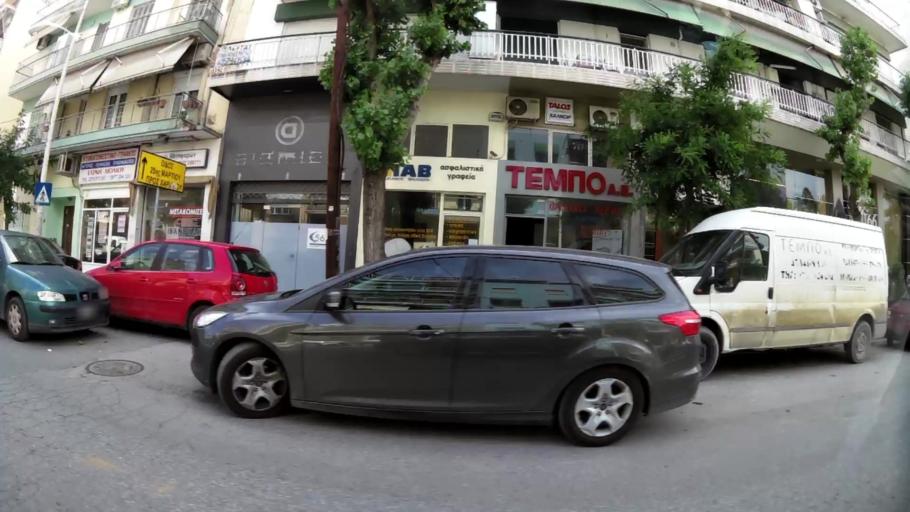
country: GR
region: Central Macedonia
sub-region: Nomos Thessalonikis
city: Kalamaria
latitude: 40.6013
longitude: 22.9592
